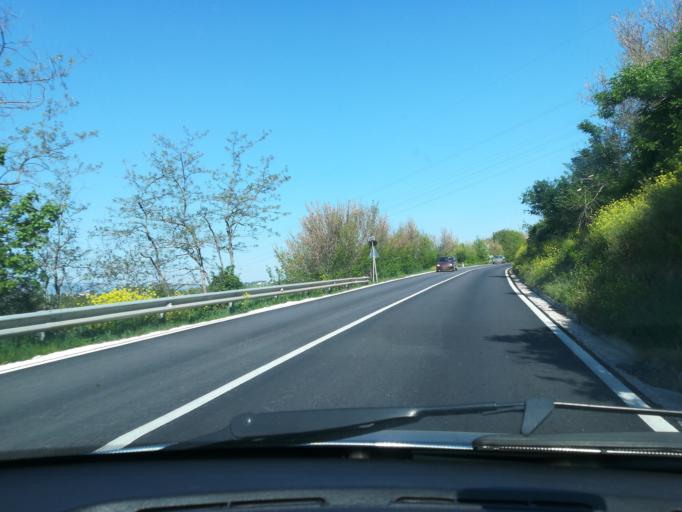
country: IT
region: The Marches
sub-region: Provincia di Macerata
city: Villa Potenza
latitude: 43.3300
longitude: 13.3875
